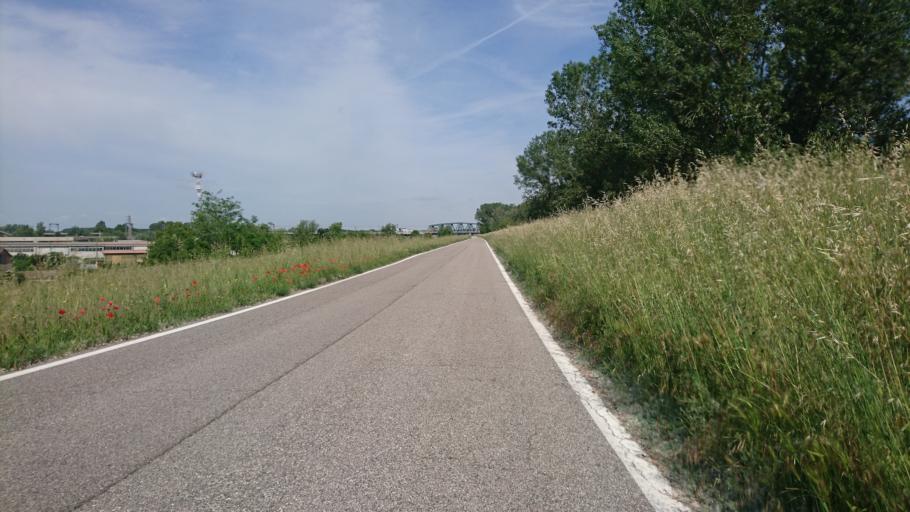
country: IT
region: Lombardy
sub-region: Provincia di Mantova
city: Revere
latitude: 45.0479
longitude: 11.1413
